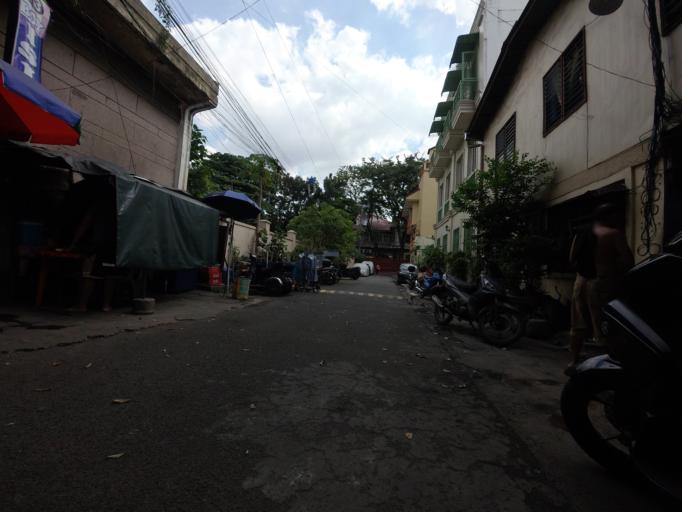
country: PH
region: Metro Manila
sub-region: City of Manila
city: Port Area
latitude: 14.5880
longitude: 120.9755
